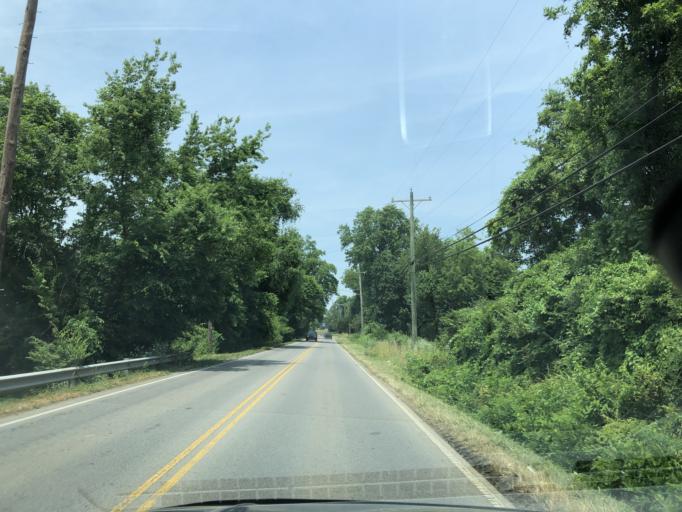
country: US
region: Tennessee
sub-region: Rutherford County
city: La Vergne
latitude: 36.0635
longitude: -86.6780
